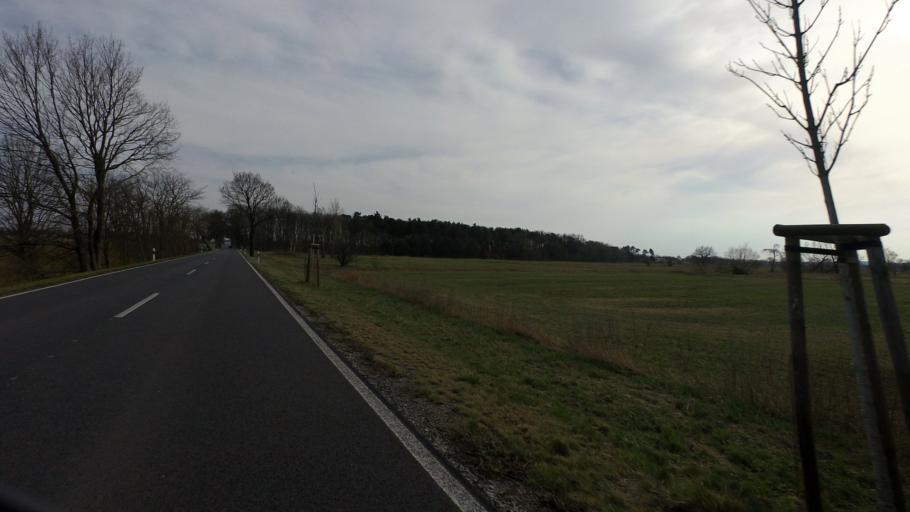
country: DE
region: Brandenburg
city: Stahnsdorf
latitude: 52.3468
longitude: 13.1969
